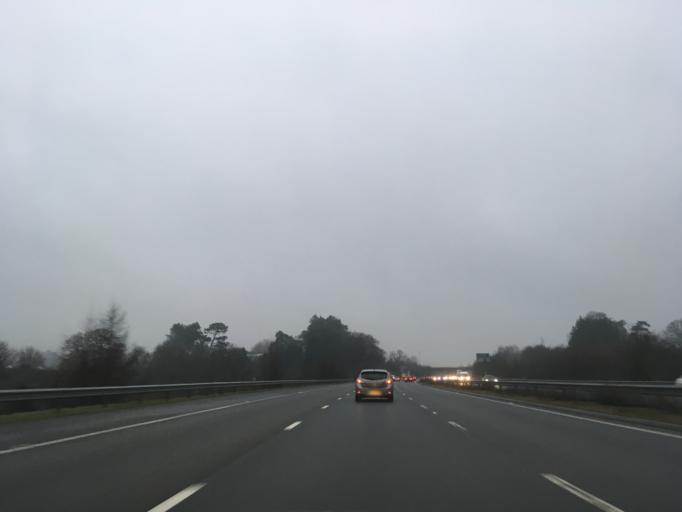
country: GB
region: Wales
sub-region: Caerphilly County Borough
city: Caerphilly
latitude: 51.5403
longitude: -3.2115
